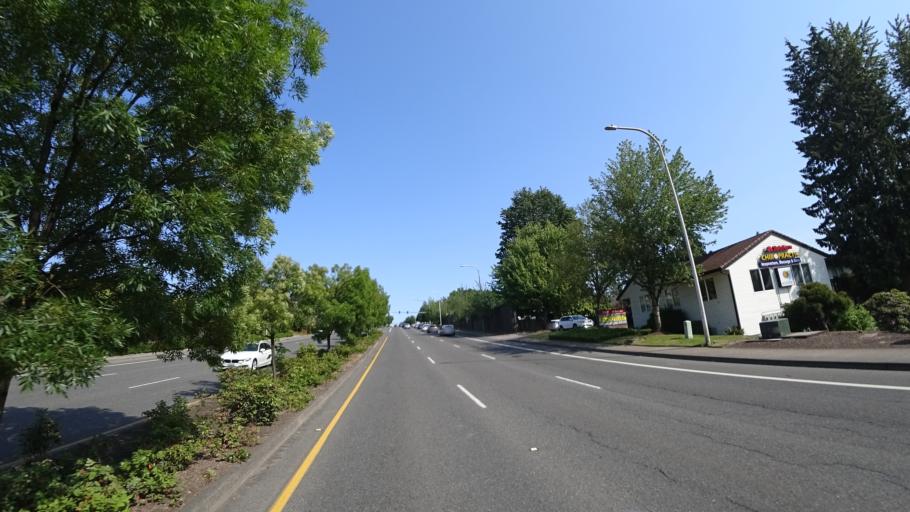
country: US
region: Oregon
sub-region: Clackamas County
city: Sunnyside
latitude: 45.4309
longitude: -122.5422
